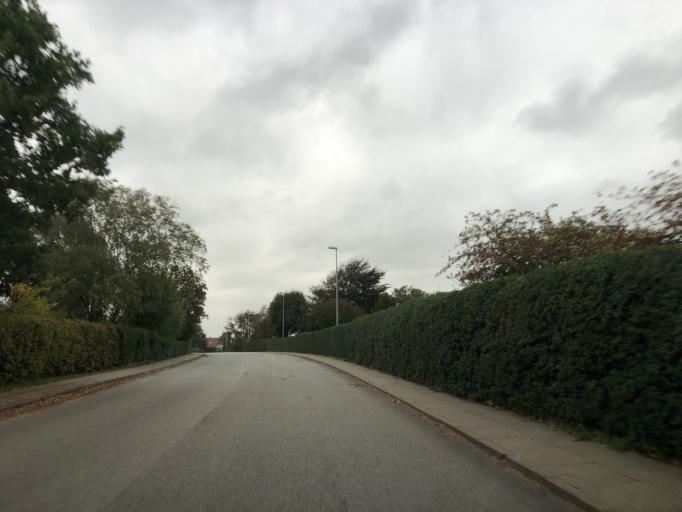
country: DK
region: Central Jutland
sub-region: Herning Kommune
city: Avlum
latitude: 56.2710
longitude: 8.7941
